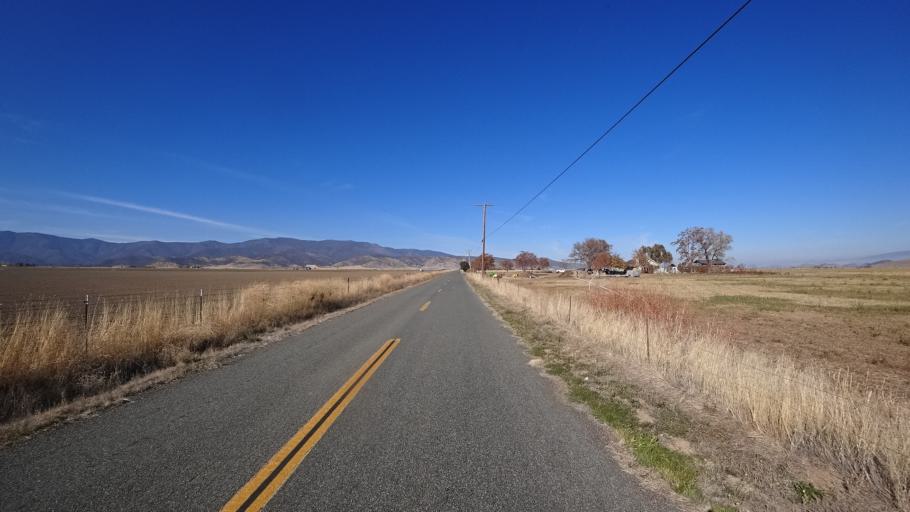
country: US
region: California
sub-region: Siskiyou County
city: Weed
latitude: 41.5389
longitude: -122.5357
